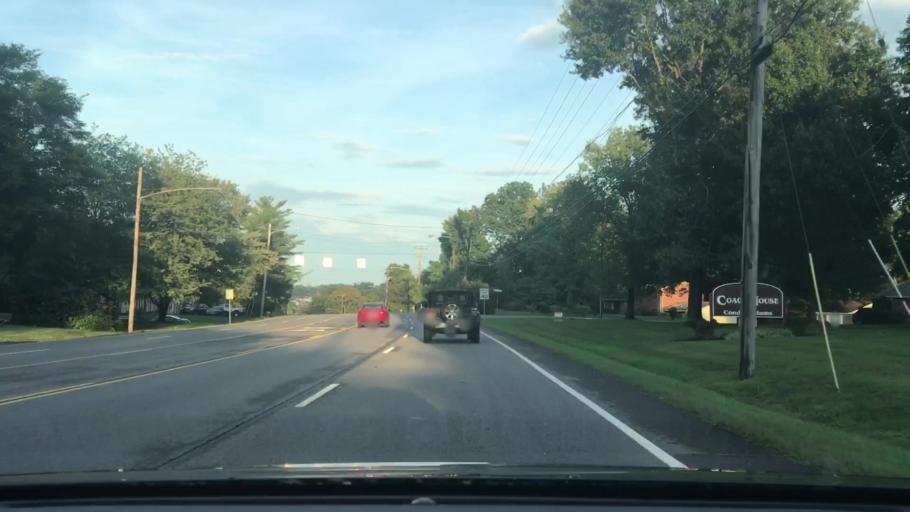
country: US
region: Tennessee
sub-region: Davidson County
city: Oak Hill
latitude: 36.0770
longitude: -86.7350
